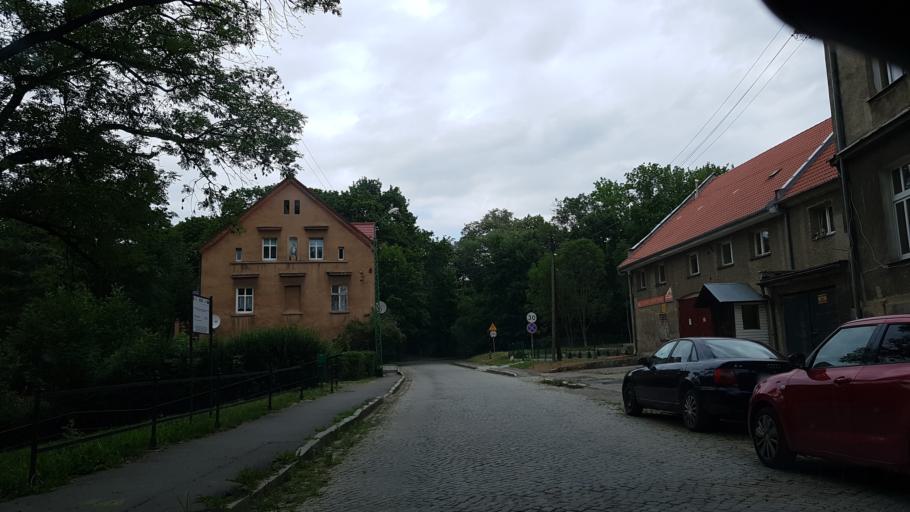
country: PL
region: Lower Silesian Voivodeship
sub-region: Powiat zabkowicki
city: Zabkowice Slaskie
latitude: 50.5896
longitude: 16.8174
